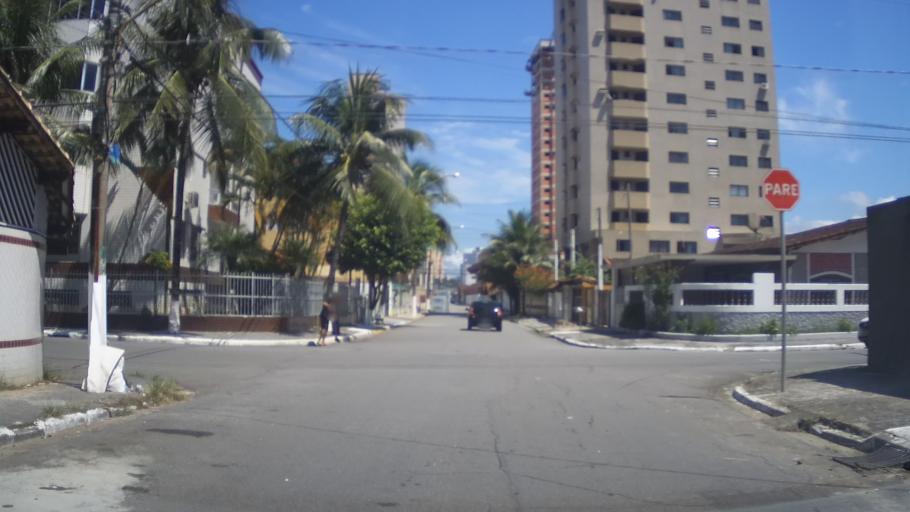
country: BR
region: Sao Paulo
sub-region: Praia Grande
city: Praia Grande
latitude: -24.0187
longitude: -46.4567
